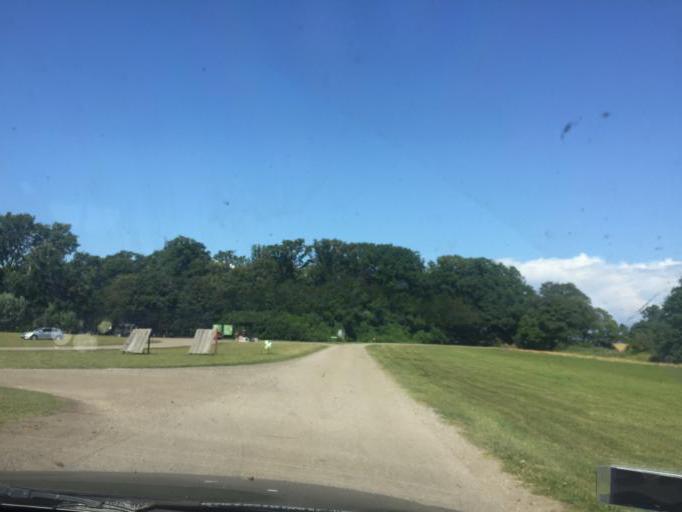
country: DK
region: Zealand
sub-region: Lolland Kommune
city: Maribo
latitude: 54.8217
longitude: 11.5155
